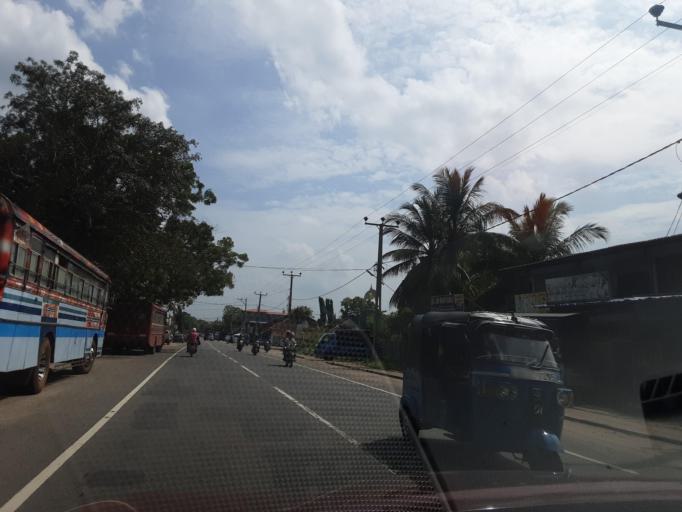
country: LK
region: Northern Province
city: Vavuniya
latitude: 8.5350
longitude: 80.4954
